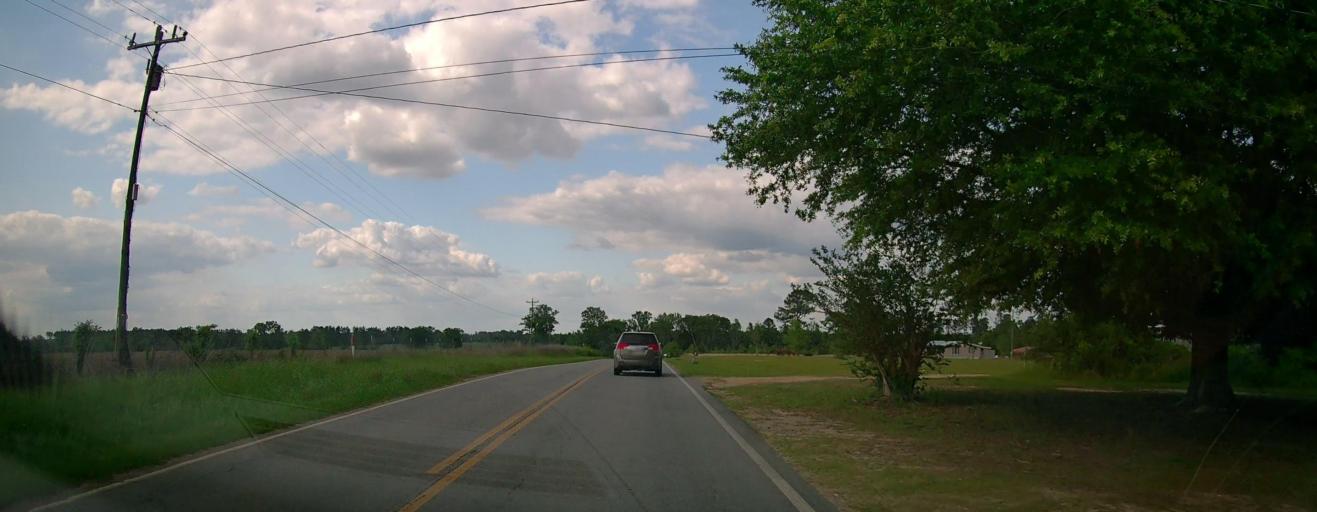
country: US
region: Georgia
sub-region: Laurens County
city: East Dublin
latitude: 32.6082
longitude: -82.8680
